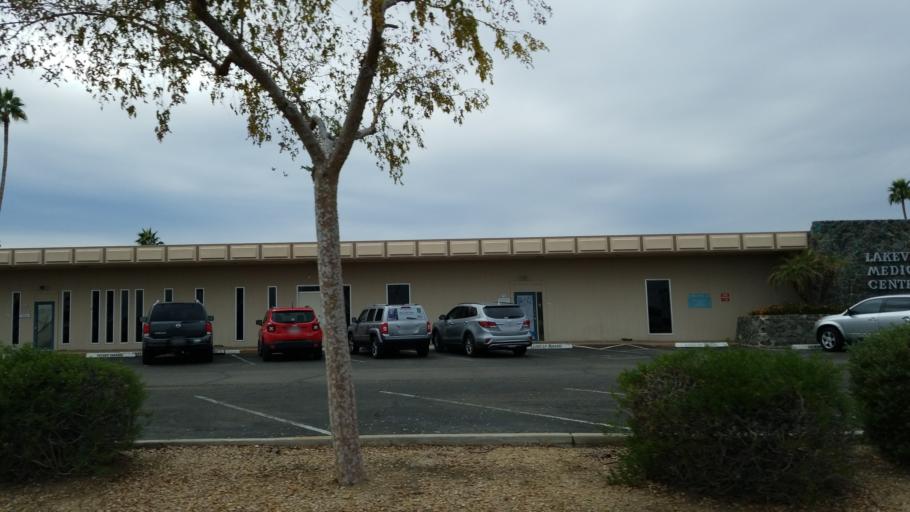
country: US
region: Arizona
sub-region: Maricopa County
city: Sun City
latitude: 33.6020
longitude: -112.2814
